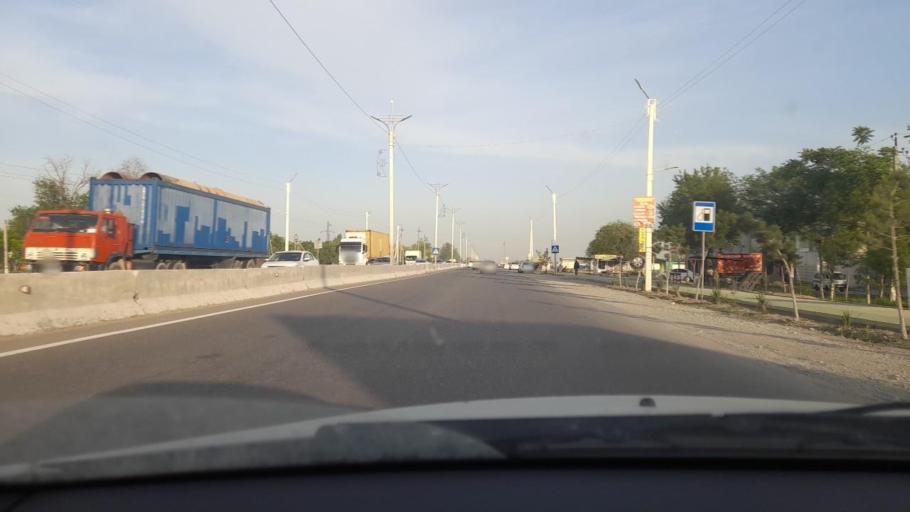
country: KZ
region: Ongtustik Qazaqstan
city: Myrzakent
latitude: 40.5403
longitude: 68.4208
